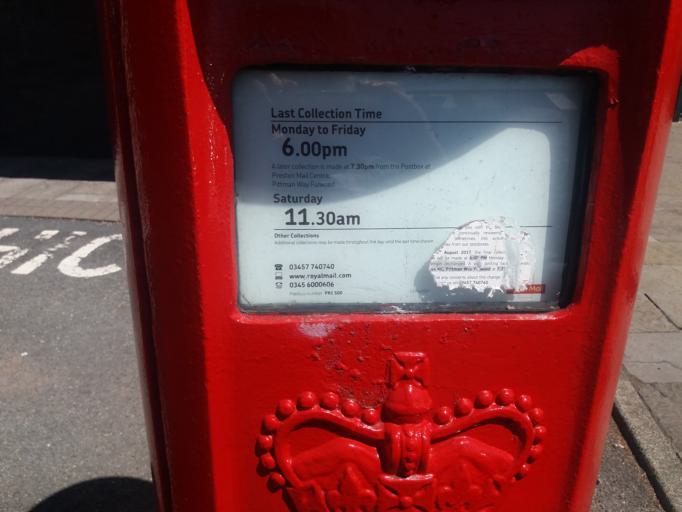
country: GB
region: England
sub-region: Lancashire
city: Preston
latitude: 53.7574
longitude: -2.7110
